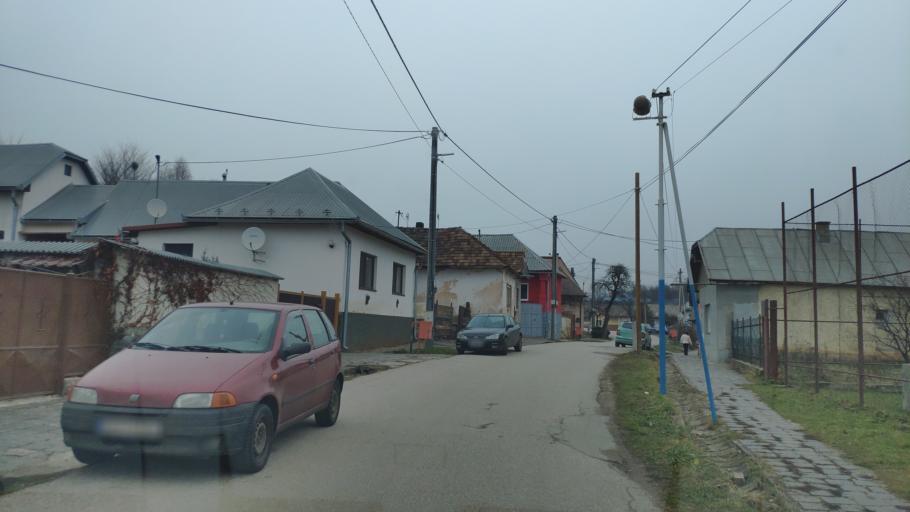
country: SK
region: Banskobystricky
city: Revuca
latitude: 48.6350
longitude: 20.2375
